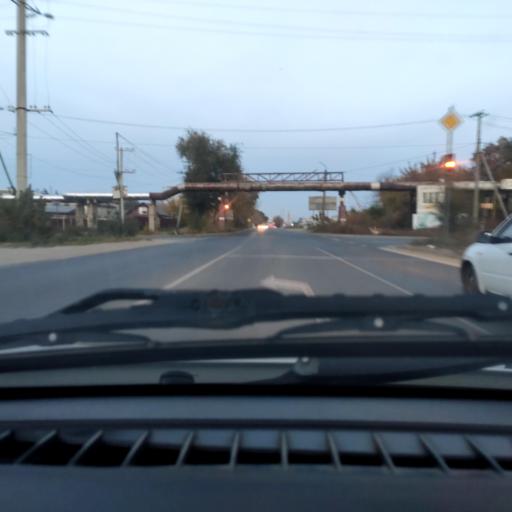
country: RU
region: Samara
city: Tol'yatti
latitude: 53.5307
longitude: 49.4631
